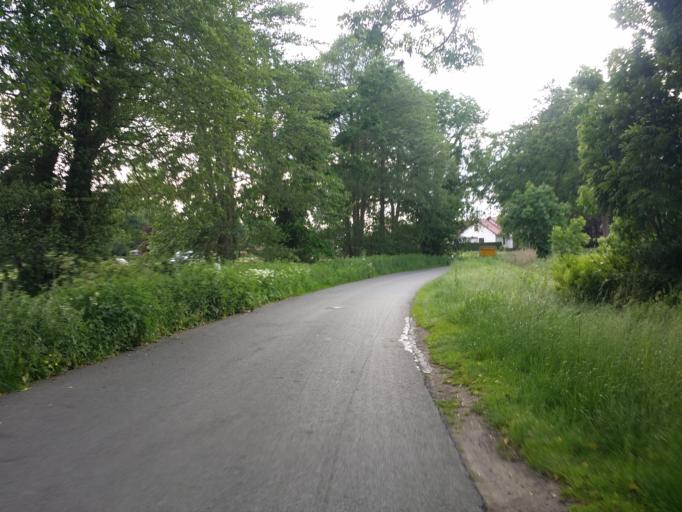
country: DE
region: Lower Saxony
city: Zetel
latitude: 53.3819
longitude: 7.9640
